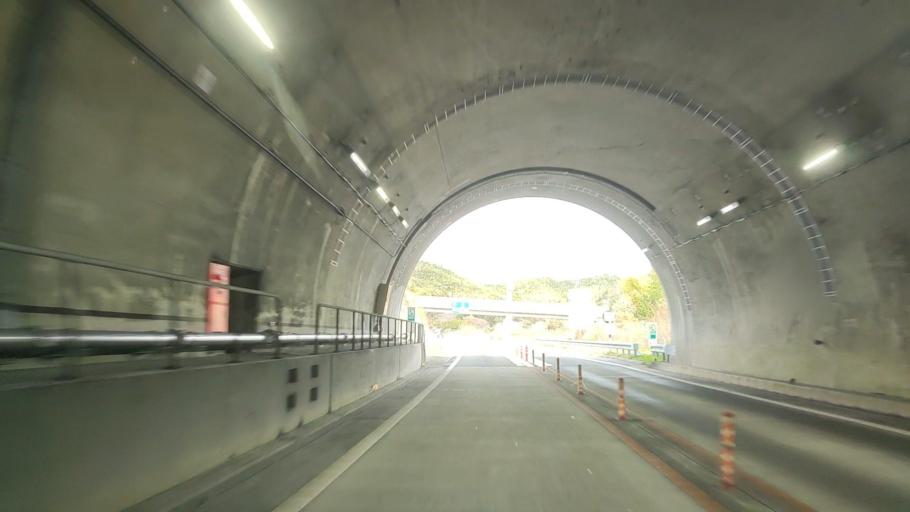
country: JP
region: Ehime
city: Hojo
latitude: 34.0875
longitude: 132.9785
